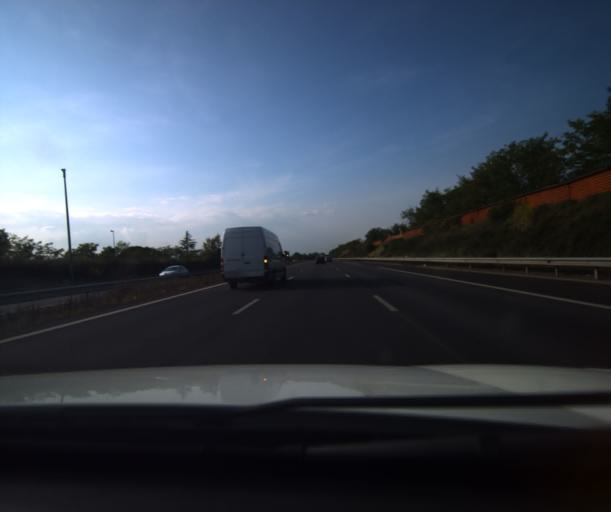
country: FR
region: Midi-Pyrenees
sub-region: Departement de la Haute-Garonne
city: Saint-Alban
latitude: 43.6920
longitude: 1.4106
